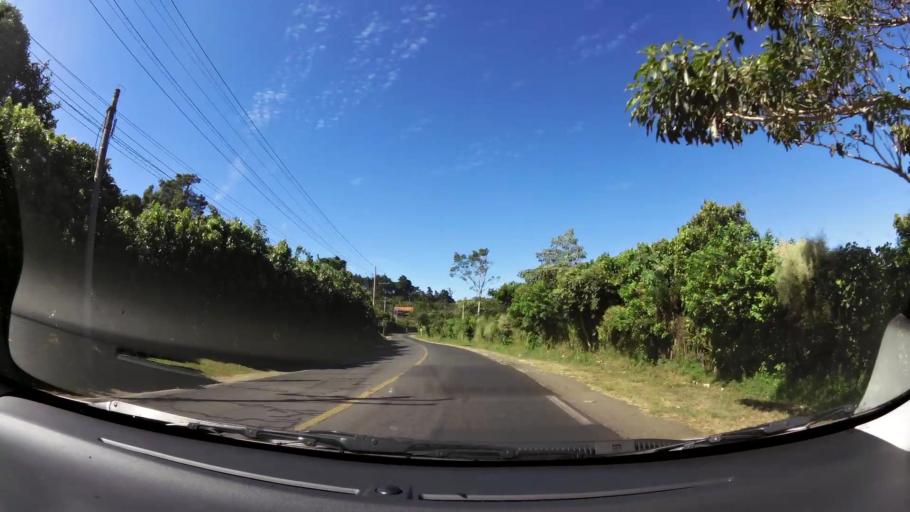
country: SV
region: Ahuachapan
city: Concepcion de Ataco
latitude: 13.8480
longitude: -89.8364
